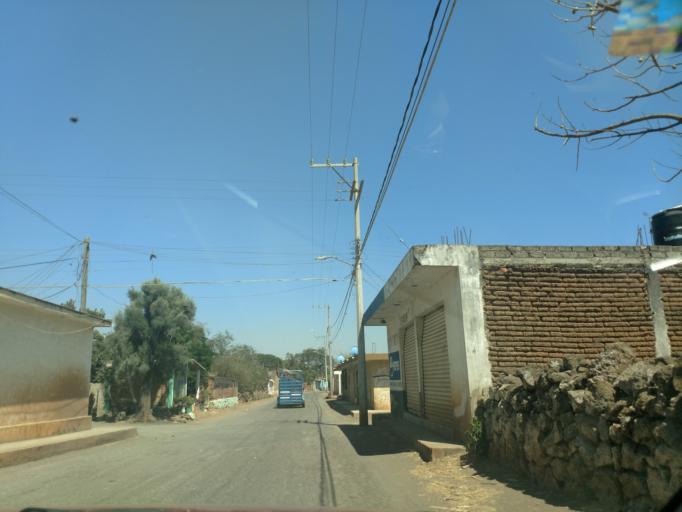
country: MX
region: Nayarit
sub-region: Tepic
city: La Corregidora
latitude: 21.5038
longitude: -104.7083
